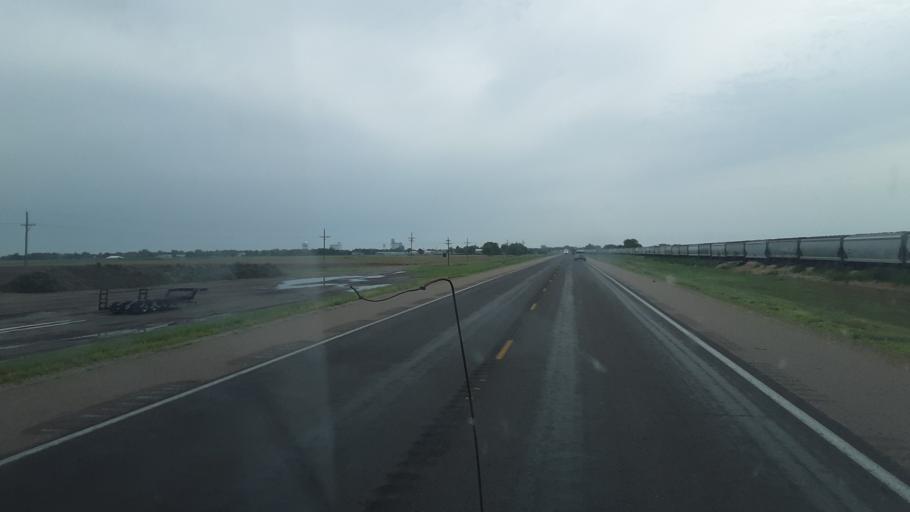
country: US
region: Kansas
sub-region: Edwards County
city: Kinsley
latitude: 37.9125
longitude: -99.4391
